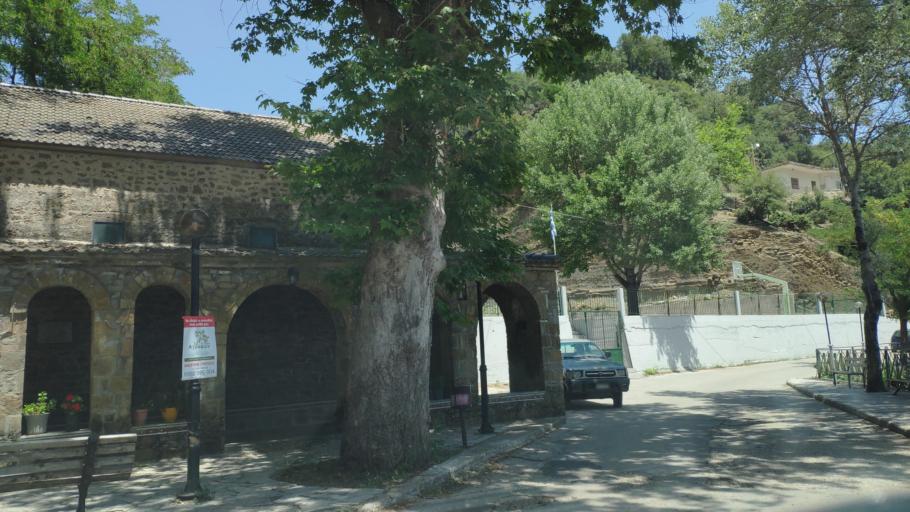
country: GR
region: Epirus
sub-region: Nomos Artas
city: Ano Kalentini
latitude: 39.2040
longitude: 21.3395
